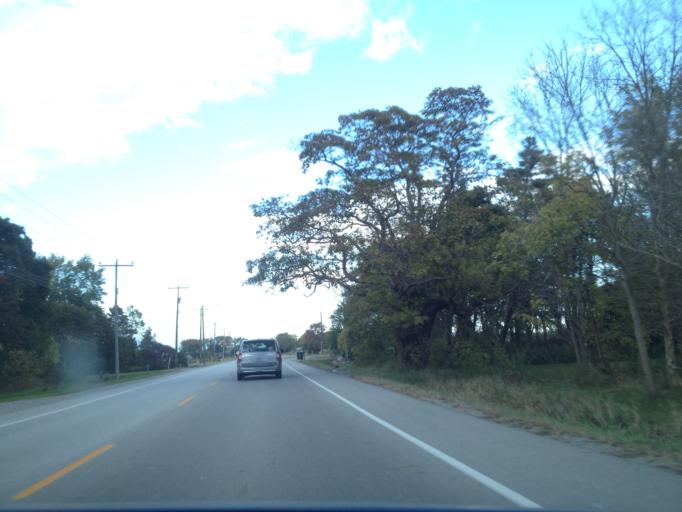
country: CA
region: Ontario
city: Amherstburg
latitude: 42.0883
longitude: -82.7359
